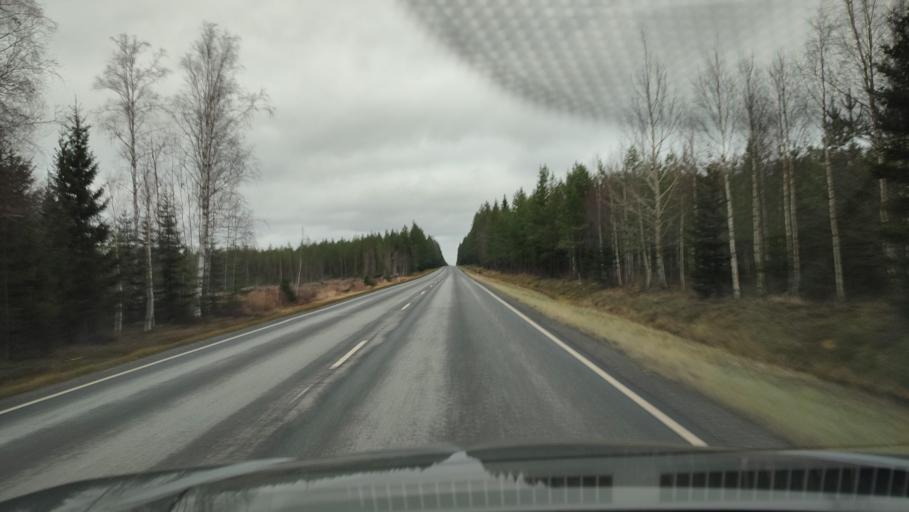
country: FI
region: Southern Ostrobothnia
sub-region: Seinaejoki
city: Kurikka
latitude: 62.5271
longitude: 22.3244
